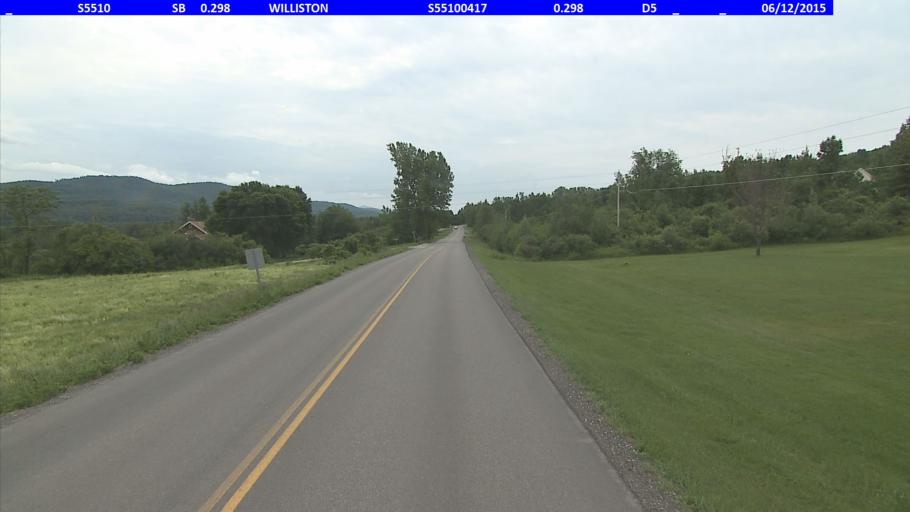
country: US
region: Vermont
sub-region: Chittenden County
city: Hinesburg
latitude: 44.3770
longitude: -73.0949
